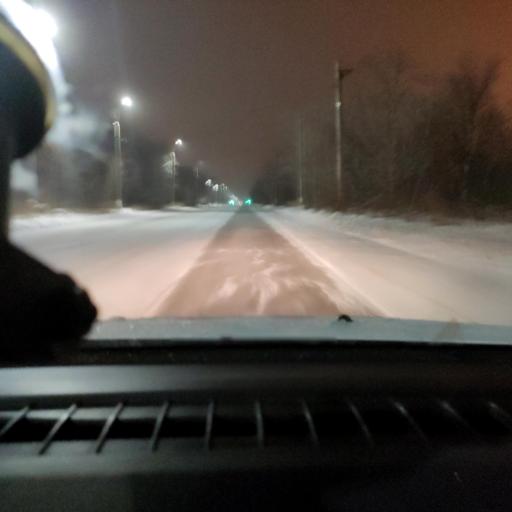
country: RU
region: Samara
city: Novokuybyshevsk
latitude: 53.0817
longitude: 49.9364
